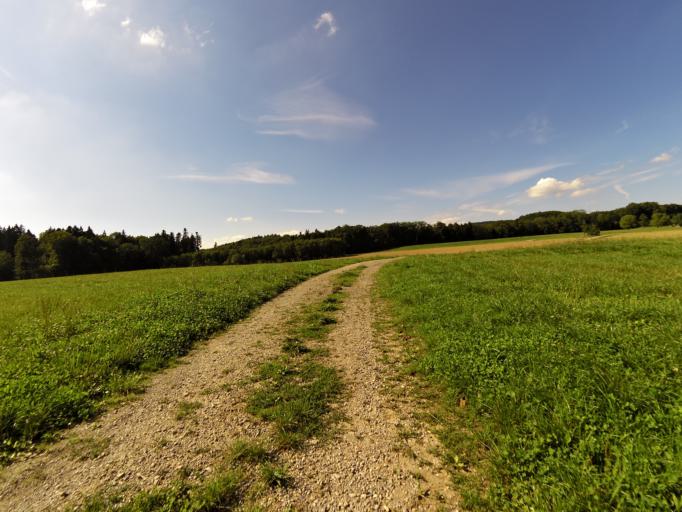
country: CH
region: Thurgau
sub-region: Frauenfeld District
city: Homburg
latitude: 47.6241
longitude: 9.0285
